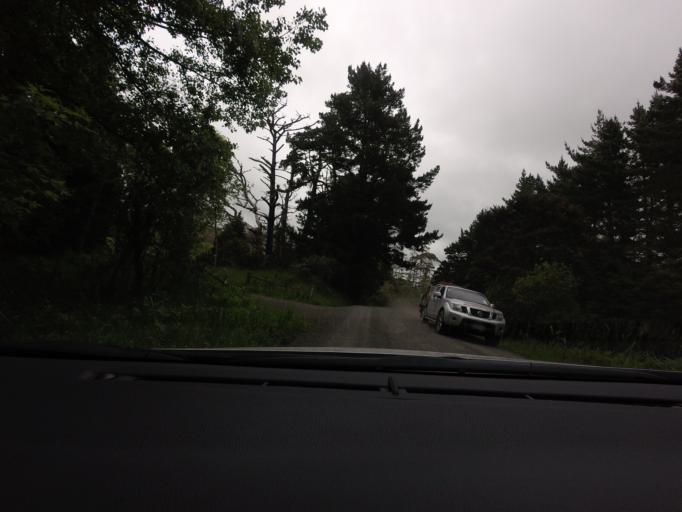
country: NZ
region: Auckland
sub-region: Auckland
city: Warkworth
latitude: -36.4783
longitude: 174.5631
